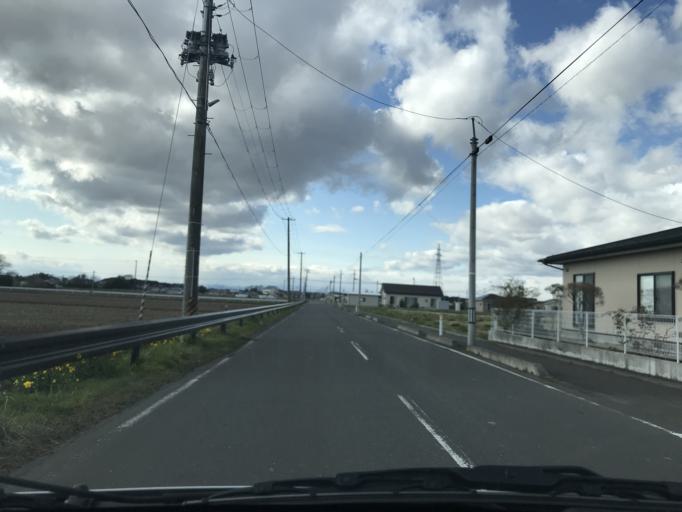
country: JP
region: Miyagi
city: Wakuya
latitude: 38.6617
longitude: 141.1855
